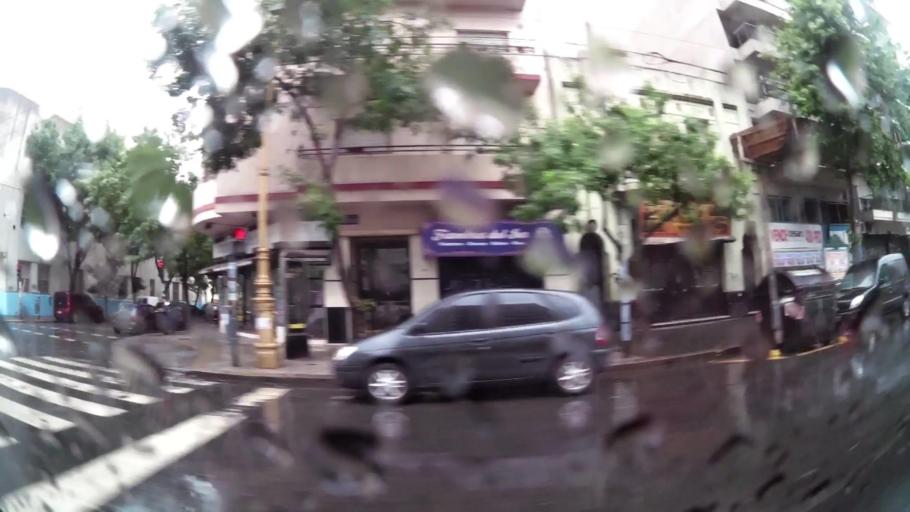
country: AR
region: Buenos Aires
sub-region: Partido de Avellaneda
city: Avellaneda
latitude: -34.6439
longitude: -58.3736
